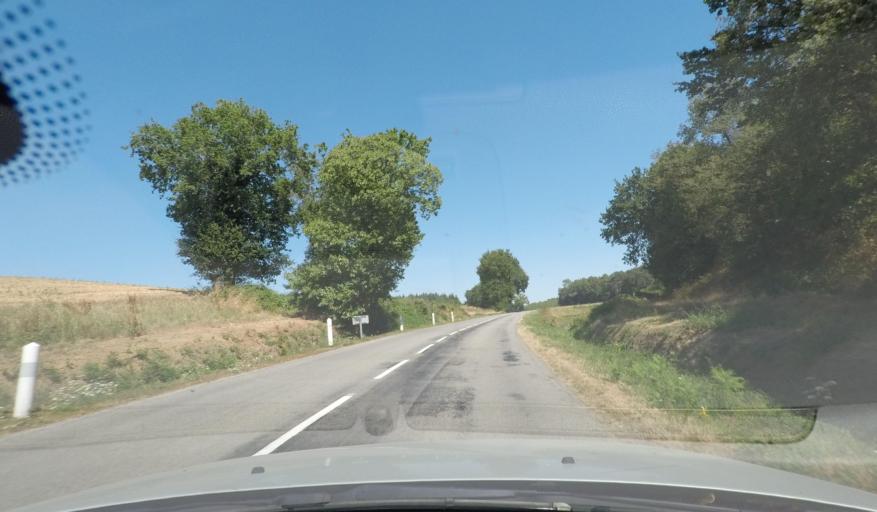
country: FR
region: Brittany
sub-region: Departement du Morbihan
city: Ruffiac
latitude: 47.8430
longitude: -2.2982
